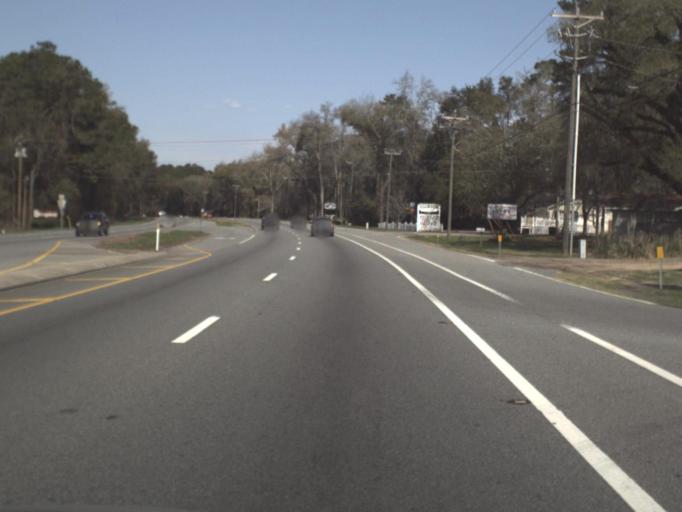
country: US
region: Florida
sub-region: Leon County
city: Tallahassee
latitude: 30.5030
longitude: -84.3294
